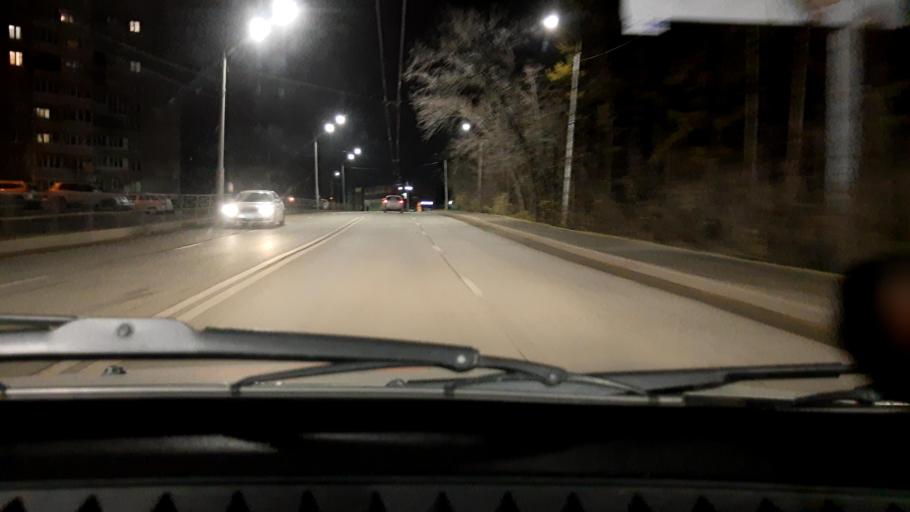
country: RU
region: Bashkortostan
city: Ufa
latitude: 54.6949
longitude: 56.0046
